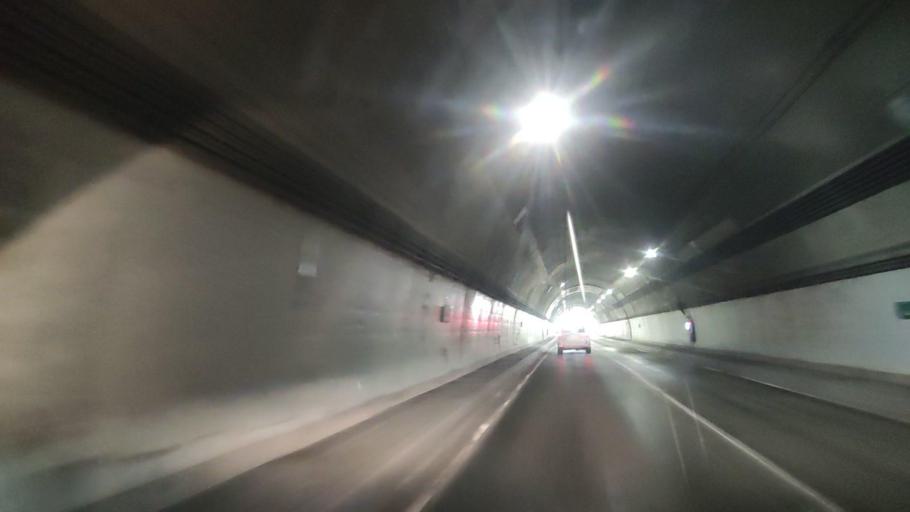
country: JP
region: Hokkaido
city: Ishikari
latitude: 43.4404
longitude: 141.4151
